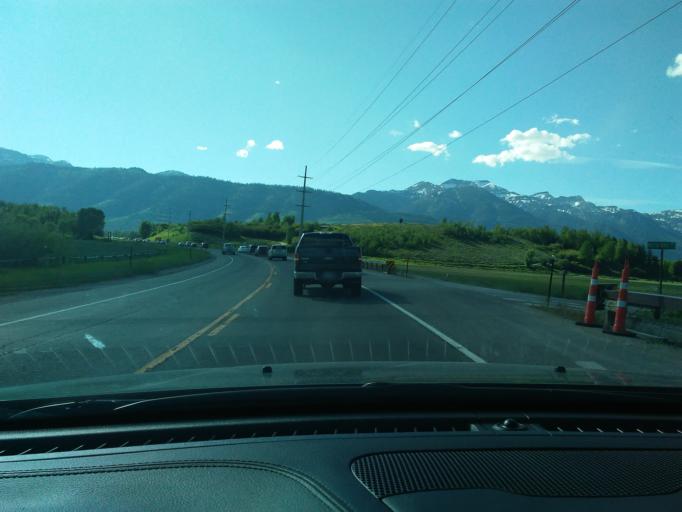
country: US
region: Wyoming
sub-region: Teton County
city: Moose Wilson Road
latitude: 43.4963
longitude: -110.8293
